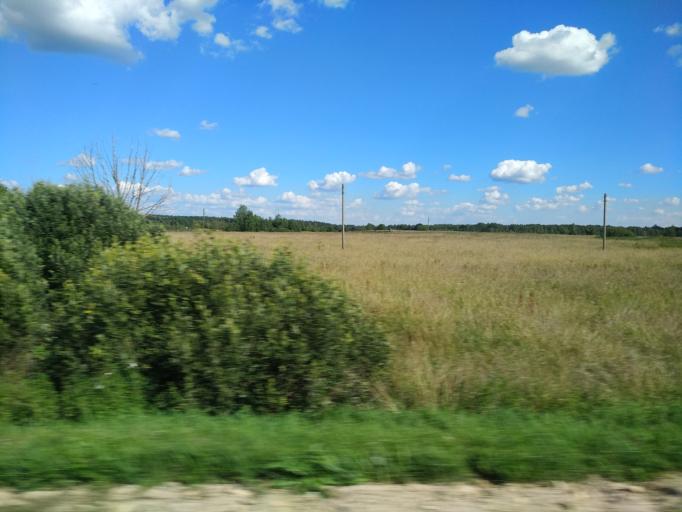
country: BY
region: Vitebsk
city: Mosar
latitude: 55.1020
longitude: 27.1997
